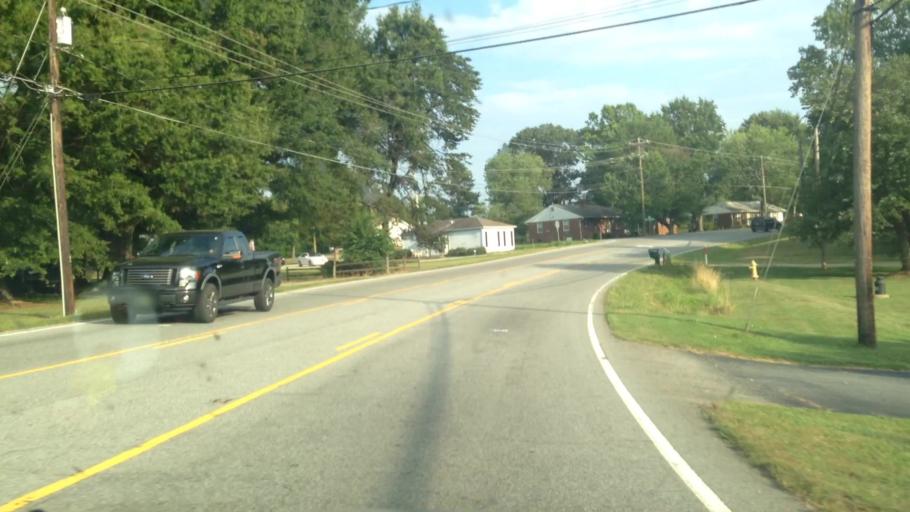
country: US
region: North Carolina
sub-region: Forsyth County
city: Kernersville
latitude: 36.0402
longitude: -80.0509
